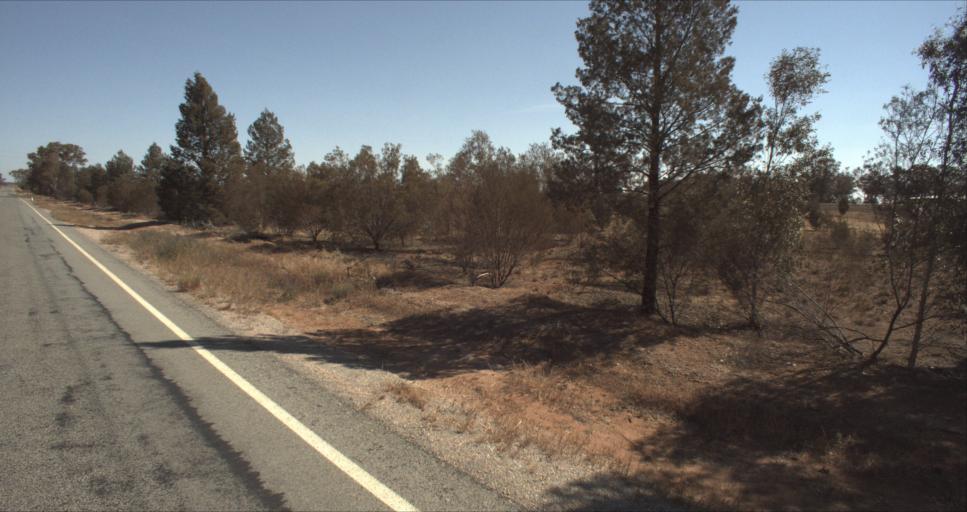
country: AU
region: New South Wales
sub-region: Leeton
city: Leeton
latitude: -34.4843
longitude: 146.4336
